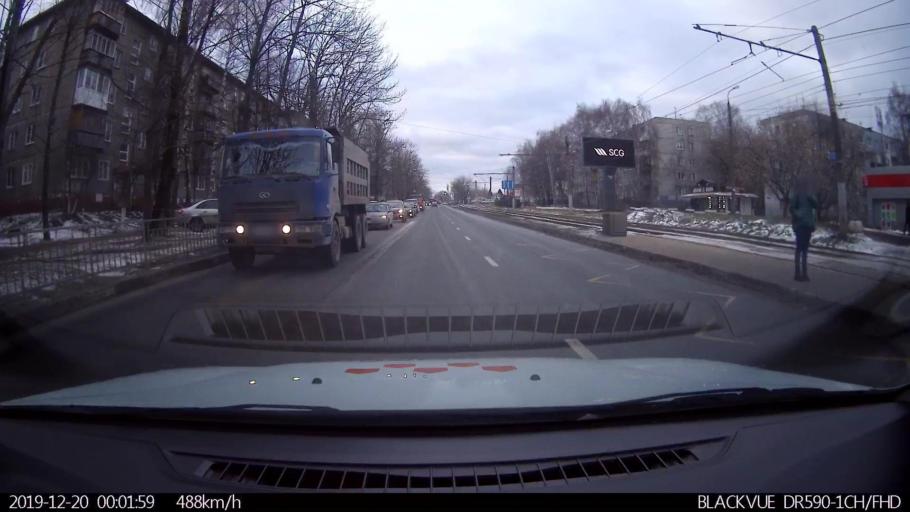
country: RU
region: Jaroslavl
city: Tutayev
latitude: 58.1763
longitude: 39.6650
